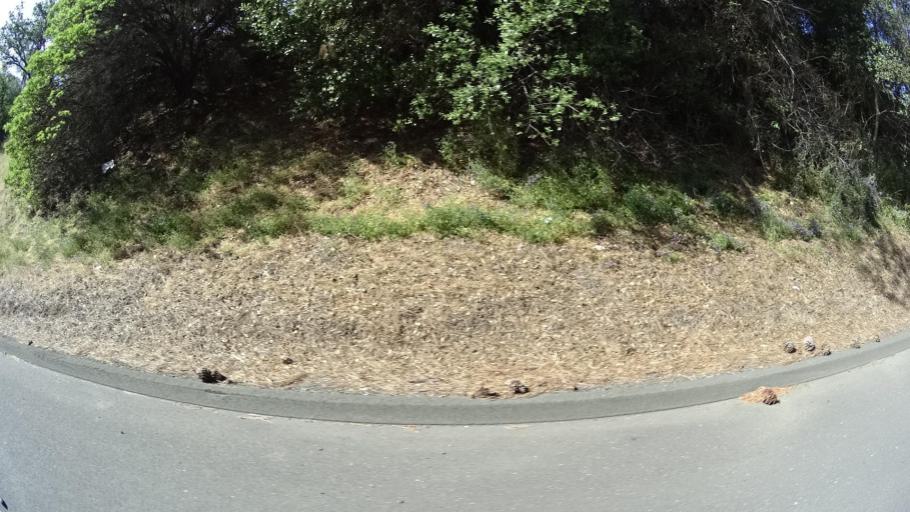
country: US
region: California
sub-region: Lake County
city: Kelseyville
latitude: 38.9748
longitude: -122.8400
